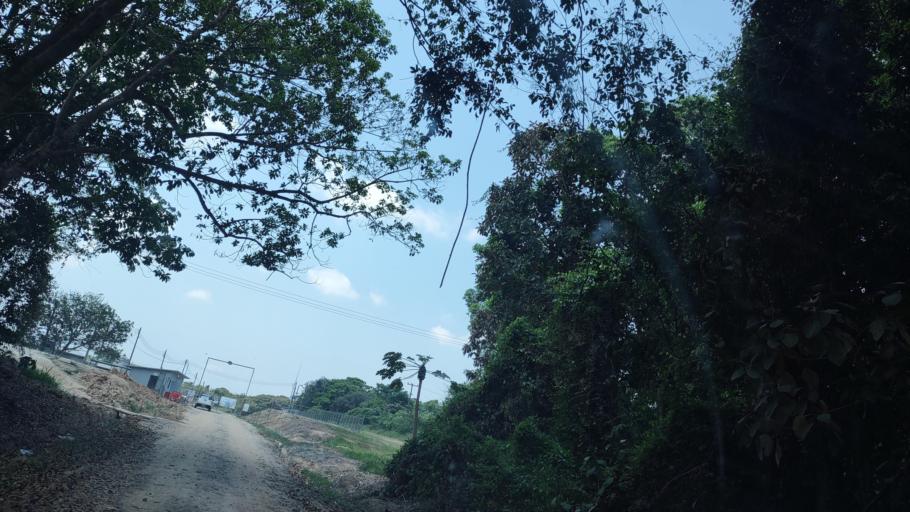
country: MX
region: Veracruz
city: Las Choapas
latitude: 17.9243
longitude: -94.1457
